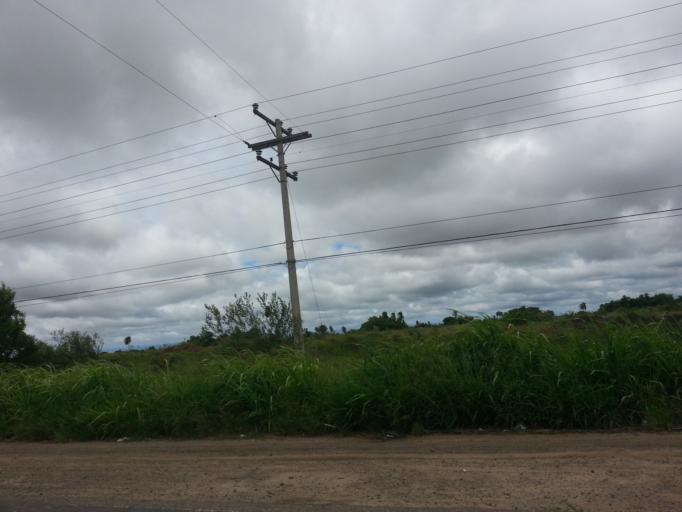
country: BO
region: Santa Cruz
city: La Belgica
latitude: -17.6228
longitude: -63.1589
